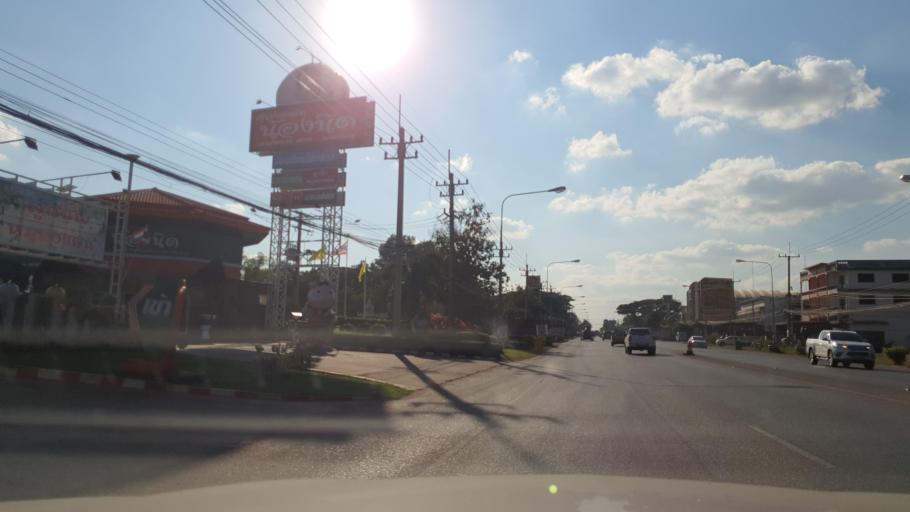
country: TH
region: Sakon Nakhon
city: Sakon Nakhon
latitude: 17.1454
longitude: 104.1270
